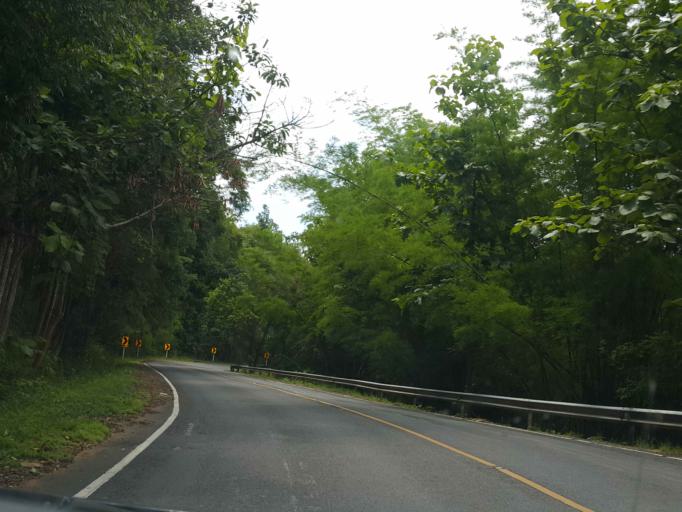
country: TH
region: Chiang Mai
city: Samoeng
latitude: 18.8187
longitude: 98.7882
